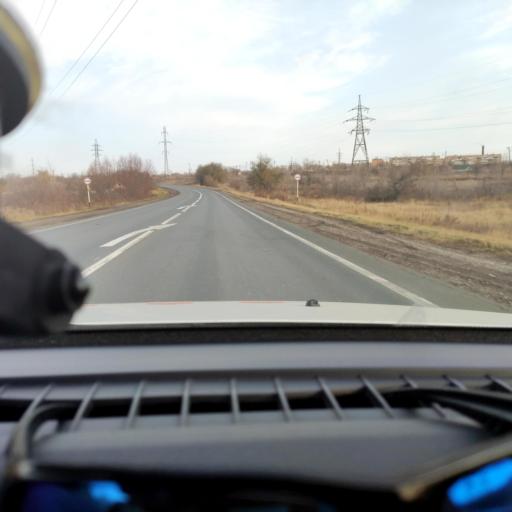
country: RU
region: Samara
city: Chapayevsk
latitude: 52.9879
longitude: 49.7652
